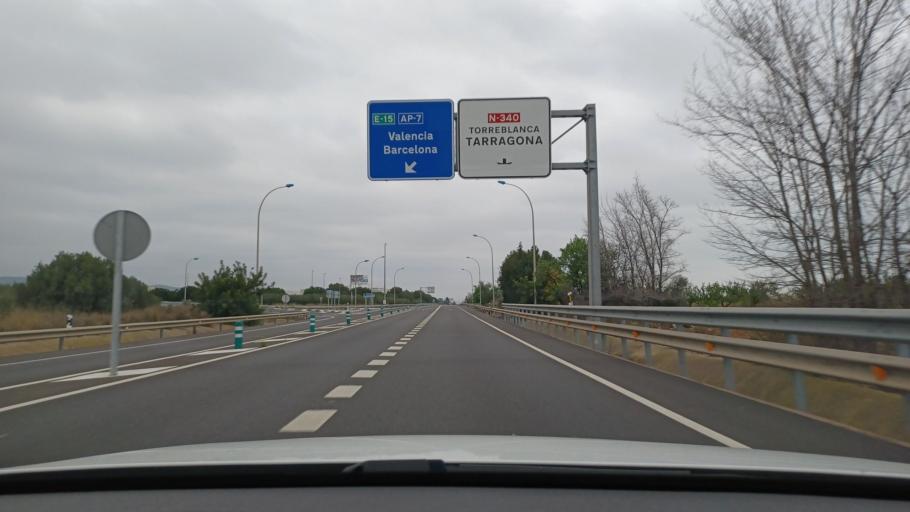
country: ES
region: Valencia
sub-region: Provincia de Castello
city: Orpesa/Oropesa del Mar
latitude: 40.1033
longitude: 0.1357
